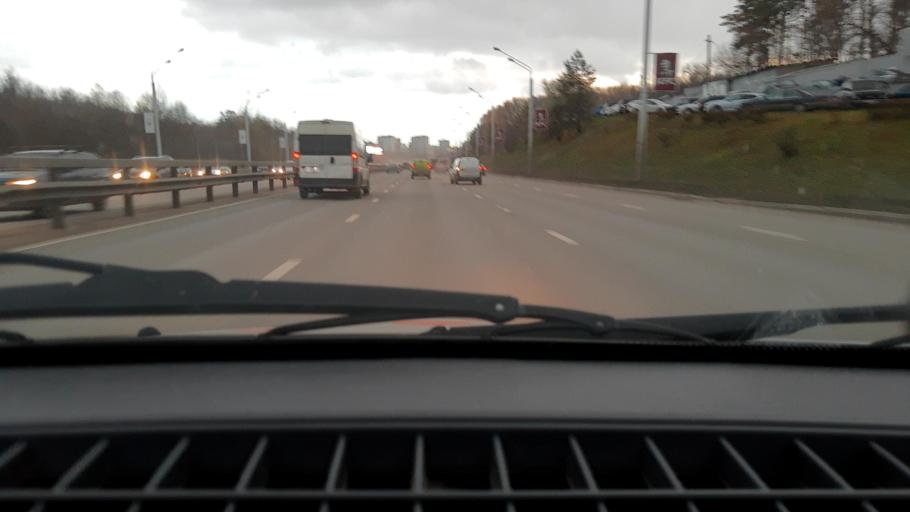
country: RU
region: Bashkortostan
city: Ufa
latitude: 54.7470
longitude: 56.0128
